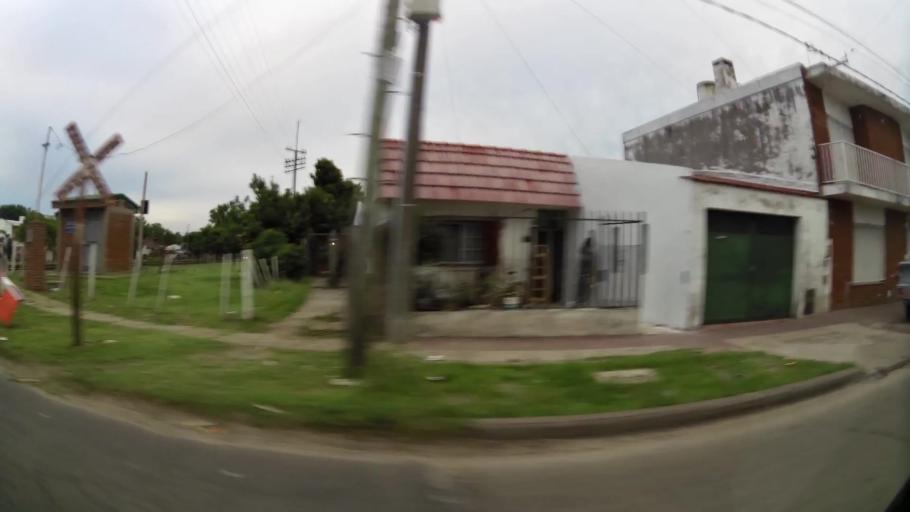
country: AR
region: Santa Fe
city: Granadero Baigorria
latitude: -32.8825
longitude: -60.7024
